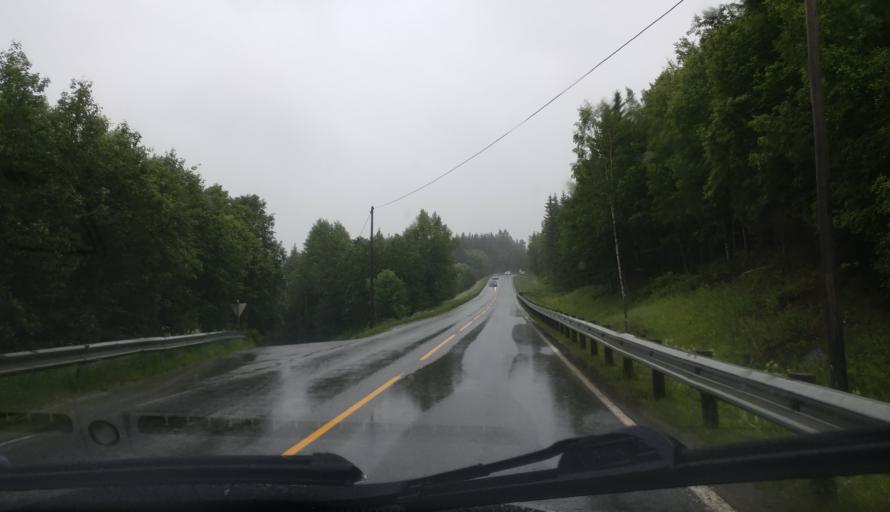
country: NO
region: Nord-Trondelag
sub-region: Stjordal
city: Stjordalshalsen
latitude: 63.4015
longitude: 10.9456
